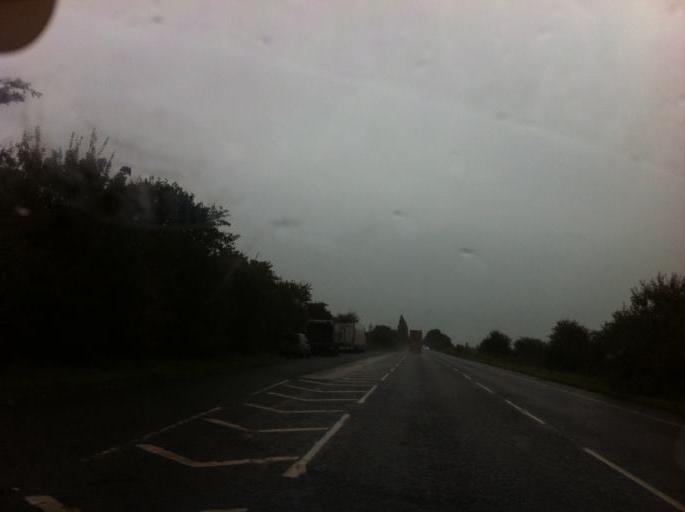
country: GB
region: England
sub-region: Lincolnshire
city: Kirton
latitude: 52.9339
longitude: -0.0484
